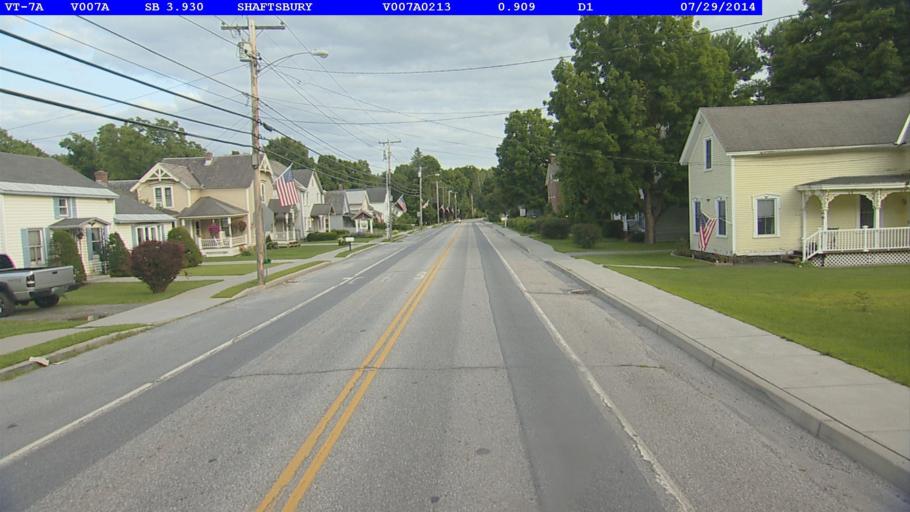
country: US
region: Vermont
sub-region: Bennington County
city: North Bennington
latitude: 42.9457
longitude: -73.2106
